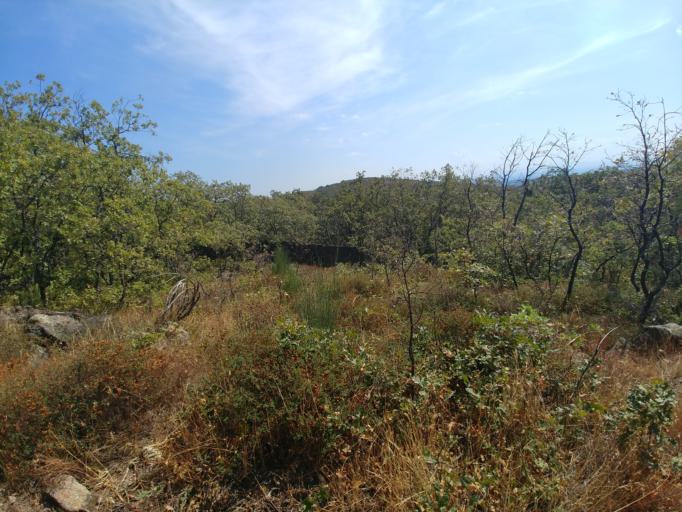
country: ES
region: Extremadura
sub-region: Provincia de Caceres
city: Garganta la Olla
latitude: 40.1116
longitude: -5.7420
